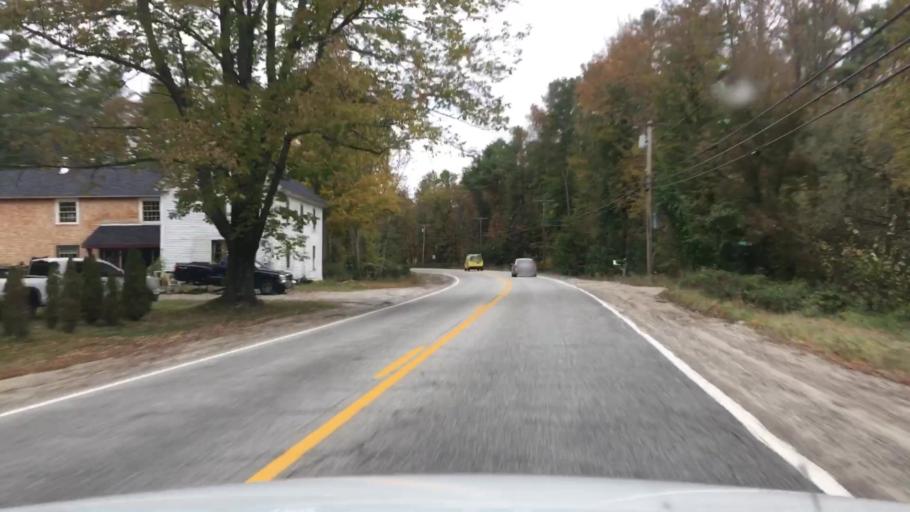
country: US
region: Maine
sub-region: Oxford County
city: Norway
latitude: 44.2192
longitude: -70.5854
